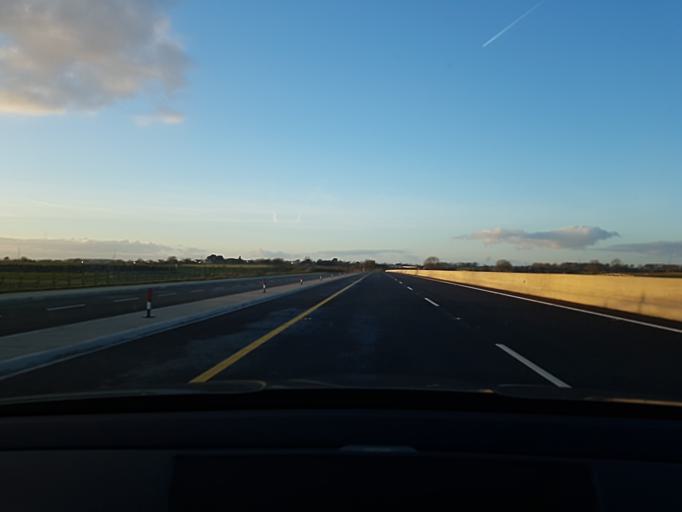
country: IE
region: Connaught
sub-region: County Galway
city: Tuam
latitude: 53.4278
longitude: -8.8360
